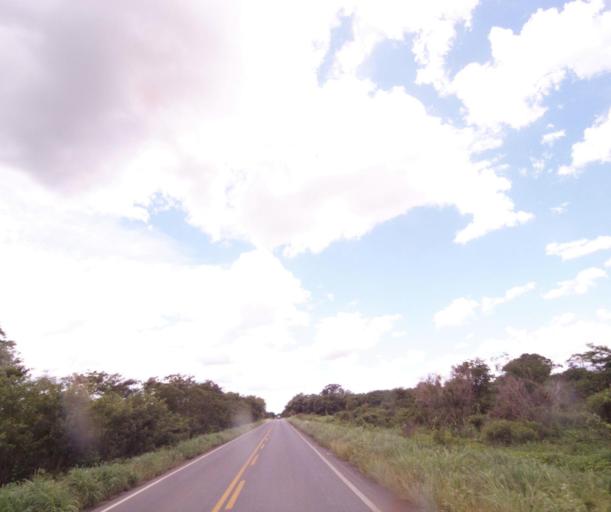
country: BR
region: Bahia
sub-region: Sao Felix Do Coribe
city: Santa Maria da Vitoria
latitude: -13.4070
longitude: -44.1605
